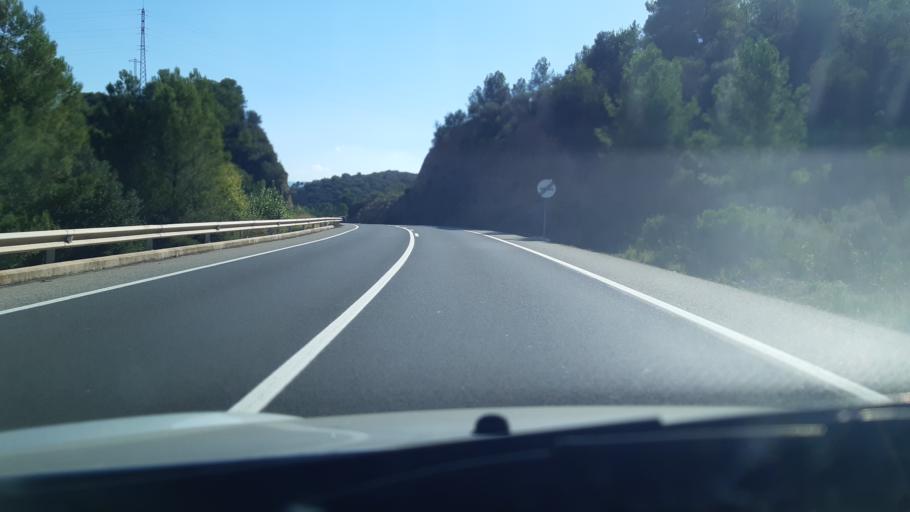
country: ES
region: Catalonia
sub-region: Provincia de Tarragona
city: Tivenys
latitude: 40.9264
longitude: 0.4866
